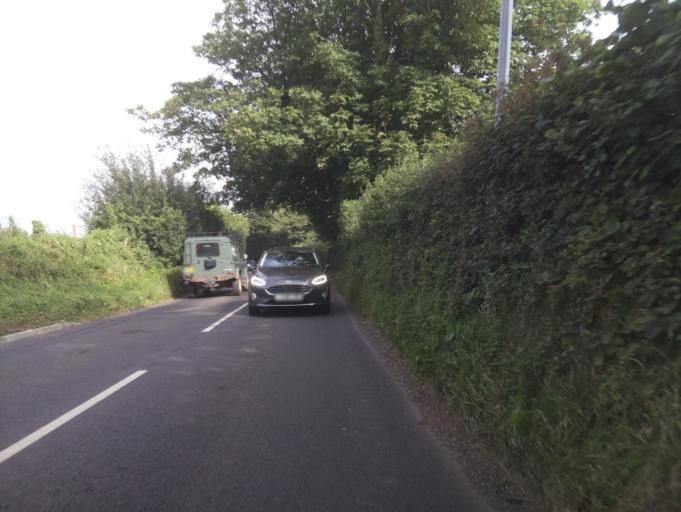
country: GB
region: England
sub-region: North Somerset
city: Winford
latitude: 51.3791
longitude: -2.6546
